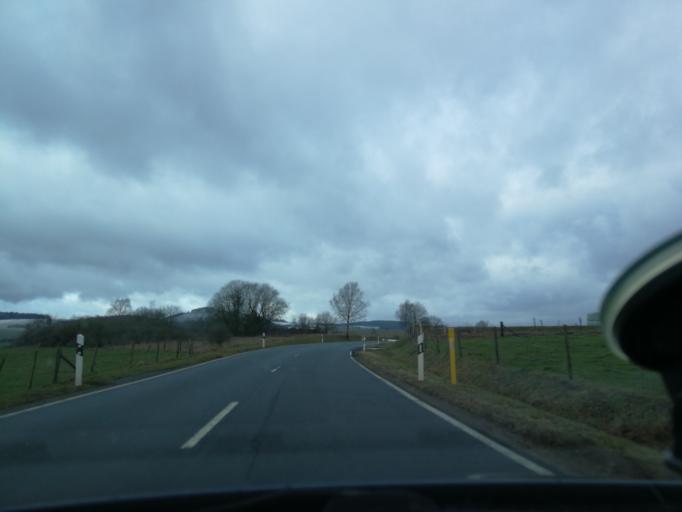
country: DE
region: Rheinland-Pfalz
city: Dreis-Bruck
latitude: 50.2583
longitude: 6.8009
